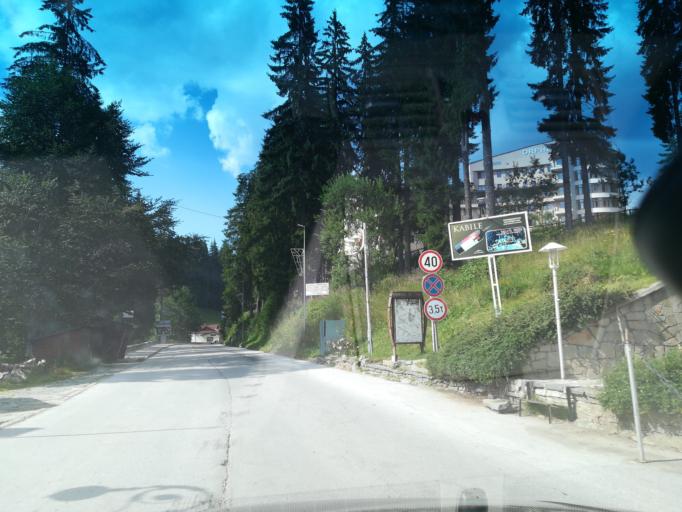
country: BG
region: Smolyan
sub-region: Obshtina Smolyan
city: Smolyan
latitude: 41.6519
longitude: 24.6942
